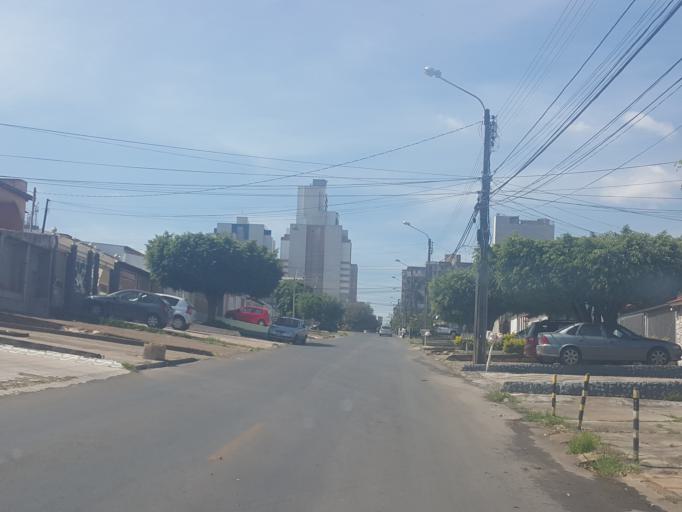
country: BR
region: Federal District
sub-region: Brasilia
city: Brasilia
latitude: -15.8255
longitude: -48.0650
